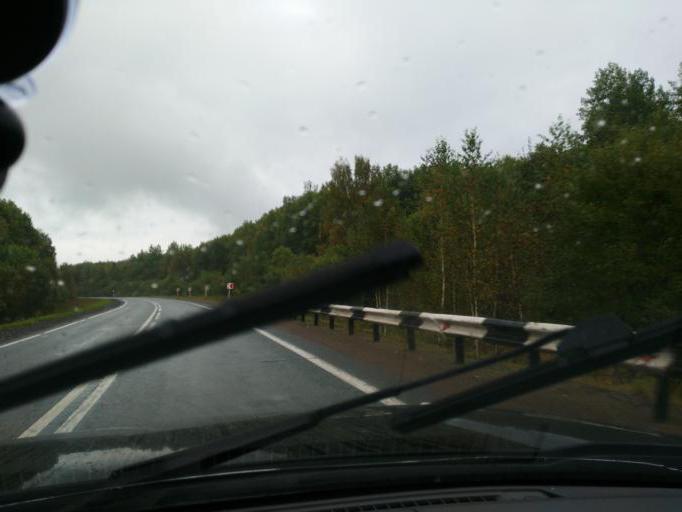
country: RU
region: Perm
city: Yugo-Kamskiy
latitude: 57.7331
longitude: 55.7056
